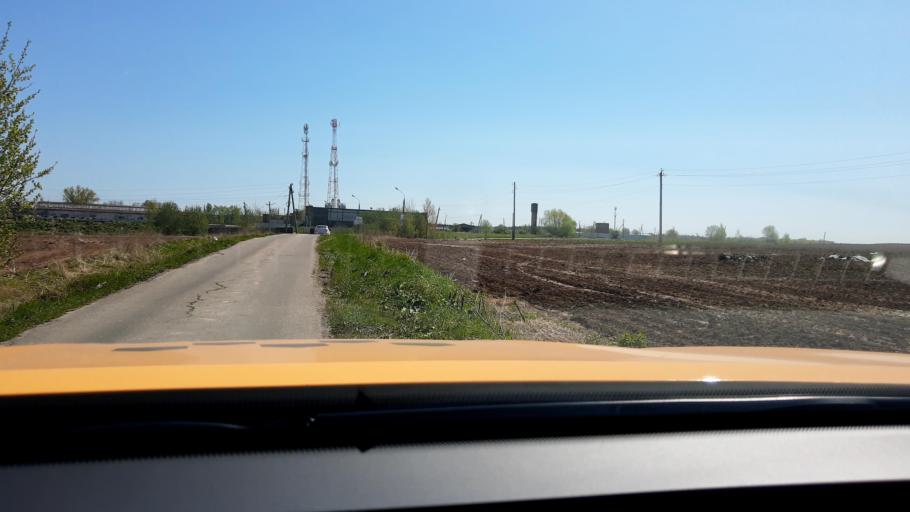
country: RU
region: Moskovskaya
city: Gorki-Leninskiye
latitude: 55.4679
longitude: 37.8323
